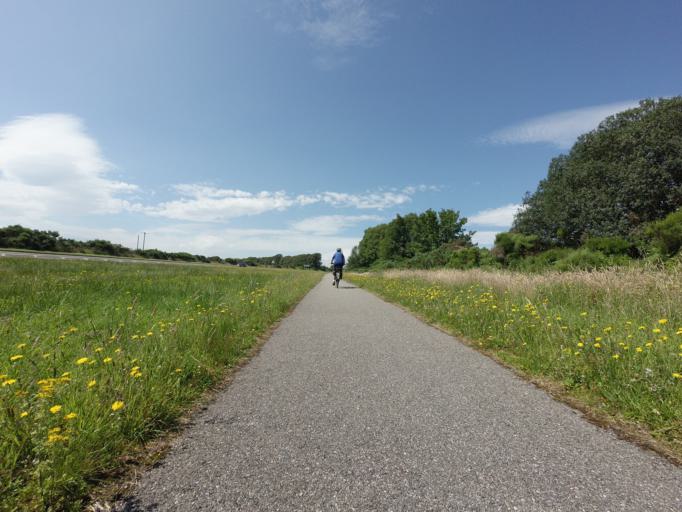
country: GB
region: Scotland
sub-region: Highland
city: Conon Bridge
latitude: 57.5382
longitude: -4.3623
